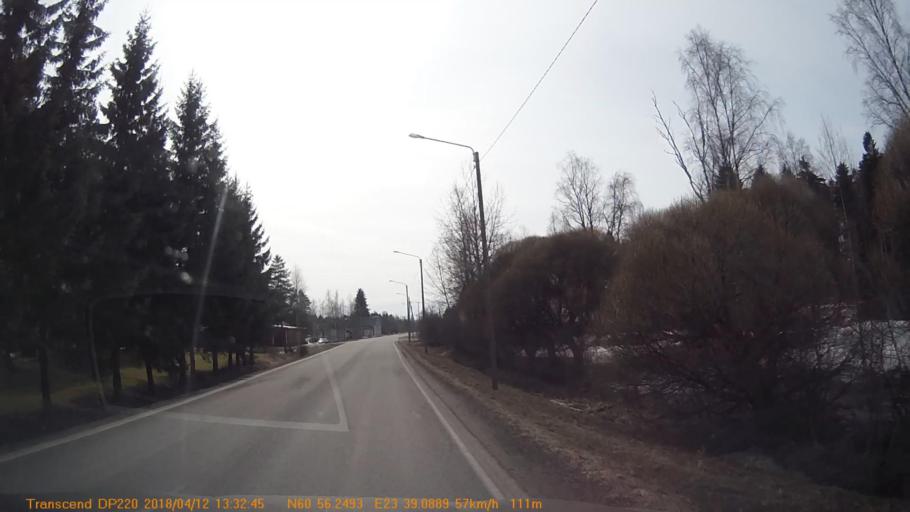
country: FI
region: Haeme
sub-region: Forssa
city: Forssa
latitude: 60.9374
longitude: 23.6514
